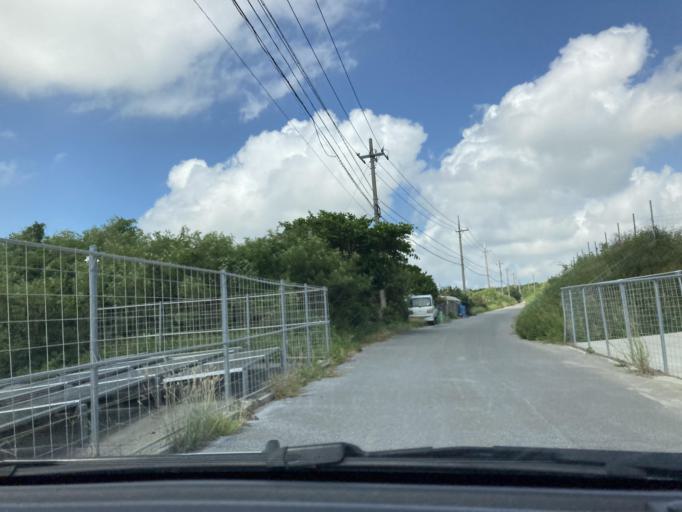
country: JP
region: Okinawa
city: Itoman
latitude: 26.1010
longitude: 127.7278
